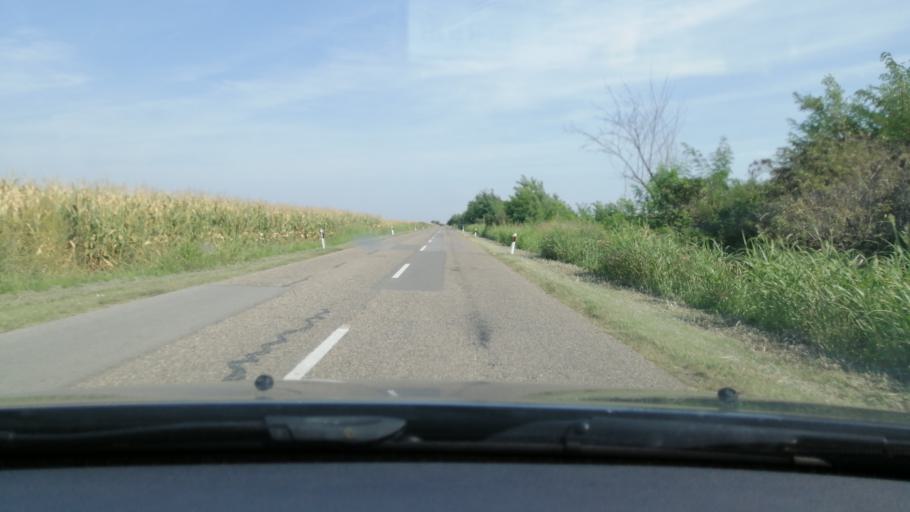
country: RS
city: Uzdin
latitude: 45.1618
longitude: 20.6172
